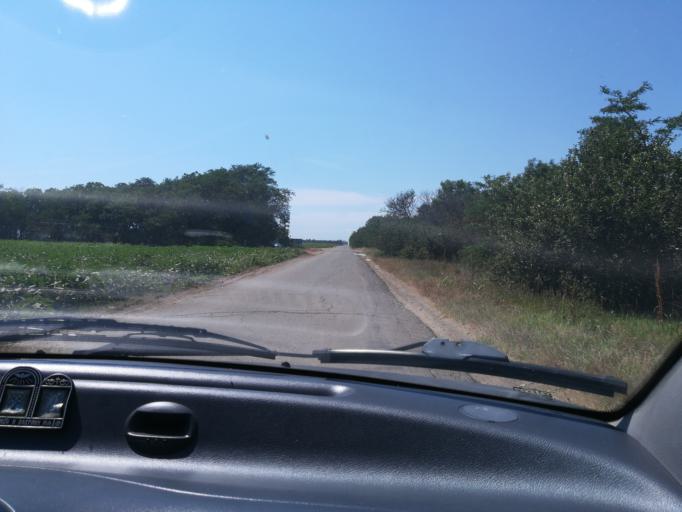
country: RU
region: Krasnodarskiy
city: Blagovetschenskaya
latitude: 45.0584
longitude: 37.1013
